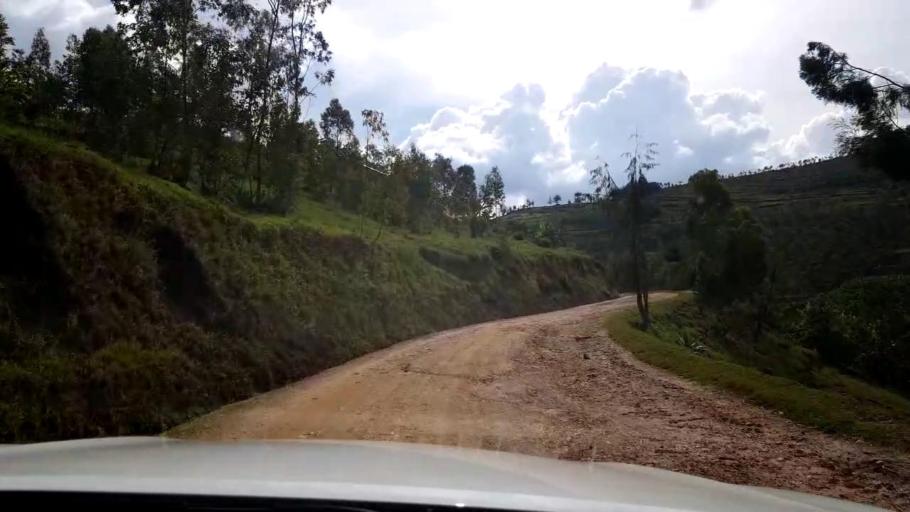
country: RW
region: Southern Province
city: Gitarama
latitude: -1.9945
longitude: 29.7116
